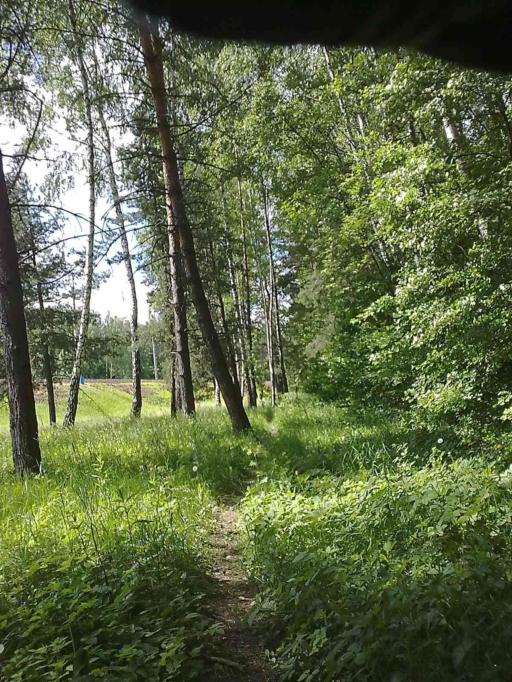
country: RU
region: Moscow
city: Novo-Peredelkino
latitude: 55.6466
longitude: 37.3034
